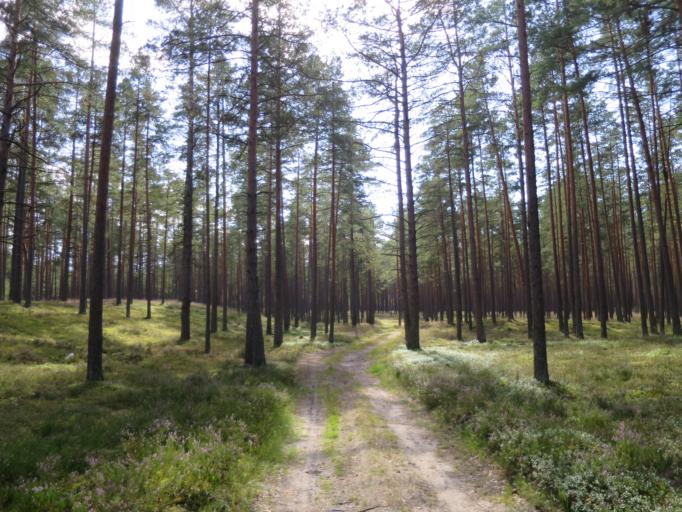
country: LV
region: Riga
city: Jaunciems
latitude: 57.0557
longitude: 24.2208
